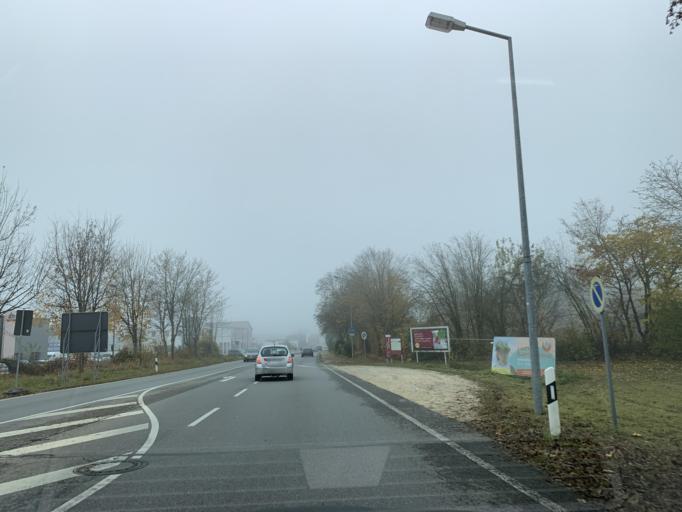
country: DE
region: Bavaria
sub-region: Lower Bavaria
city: Kelheim
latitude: 48.9221
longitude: 11.8826
